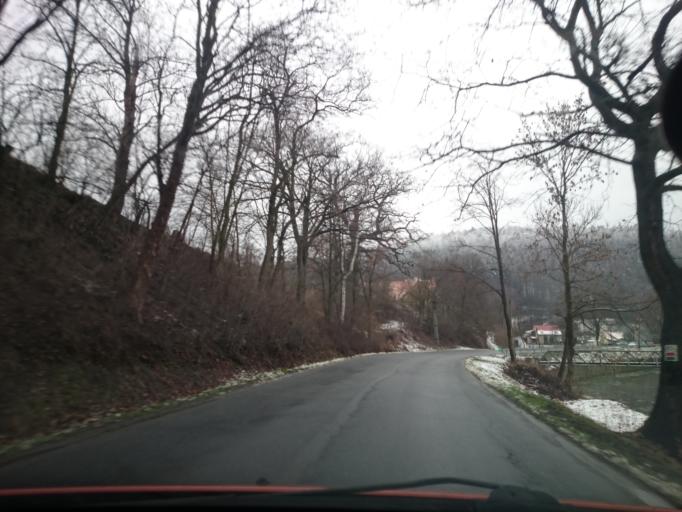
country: PL
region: Lower Silesian Voivodeship
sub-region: Powiat klodzki
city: Klodzko
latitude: 50.3968
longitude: 16.6257
